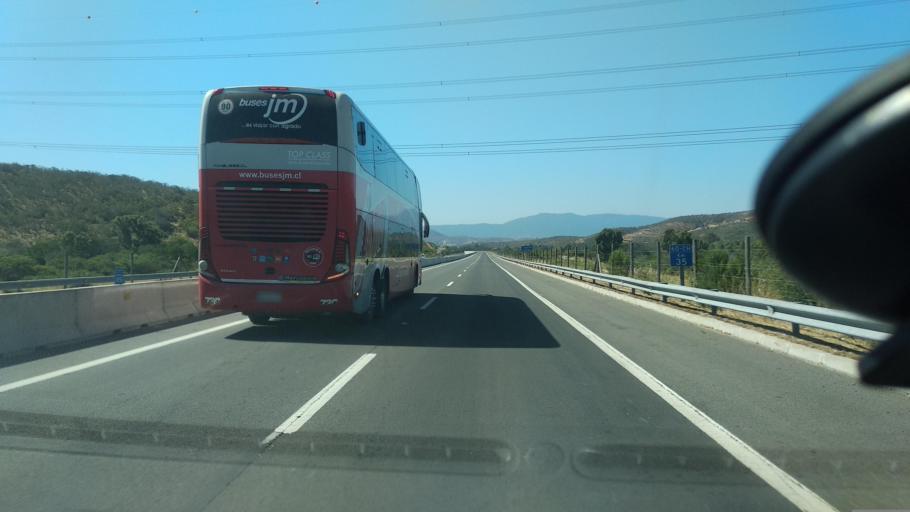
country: CL
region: Valparaiso
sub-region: Provincia de Marga Marga
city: Limache
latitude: -33.0239
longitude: -71.3190
